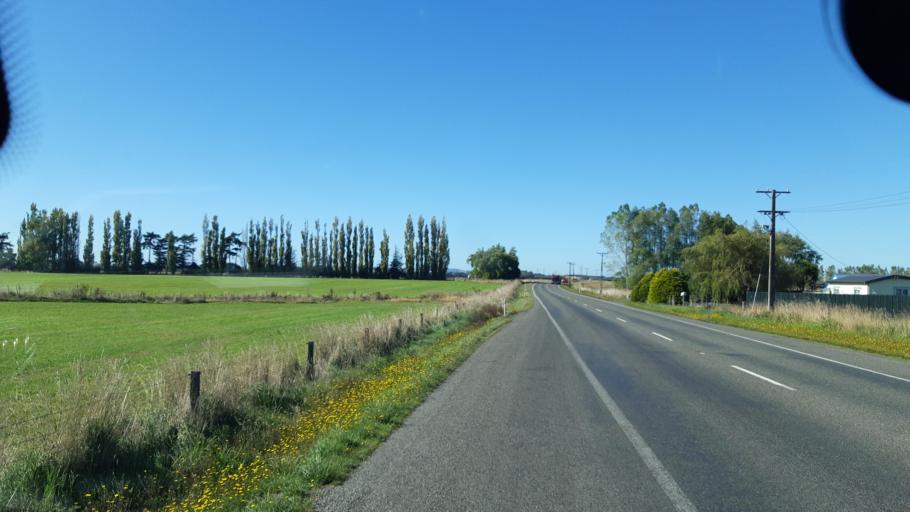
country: NZ
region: Southland
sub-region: Southland District
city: Winton
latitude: -46.1254
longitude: 168.2538
